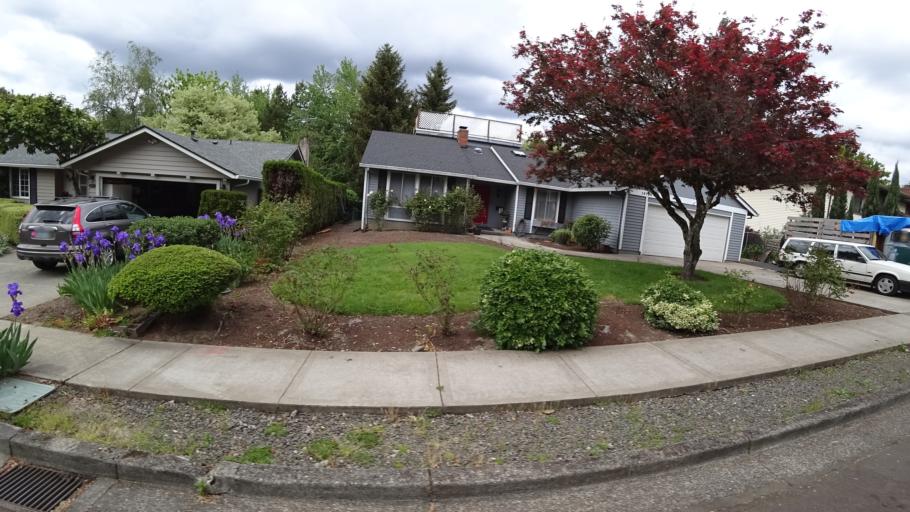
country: US
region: Oregon
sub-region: Washington County
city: Beaverton
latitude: 45.4791
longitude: -122.8283
